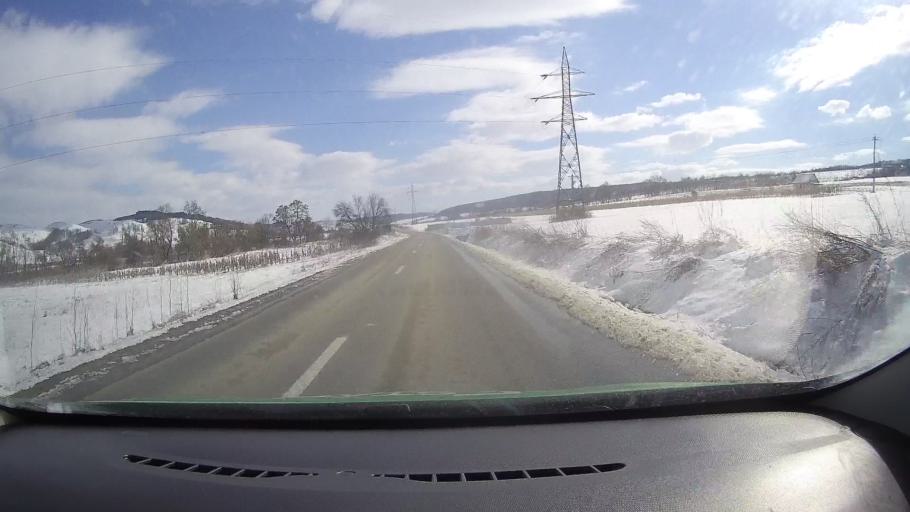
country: RO
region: Sibiu
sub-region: Comuna Barghis
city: Barghis
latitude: 45.9788
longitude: 24.5413
